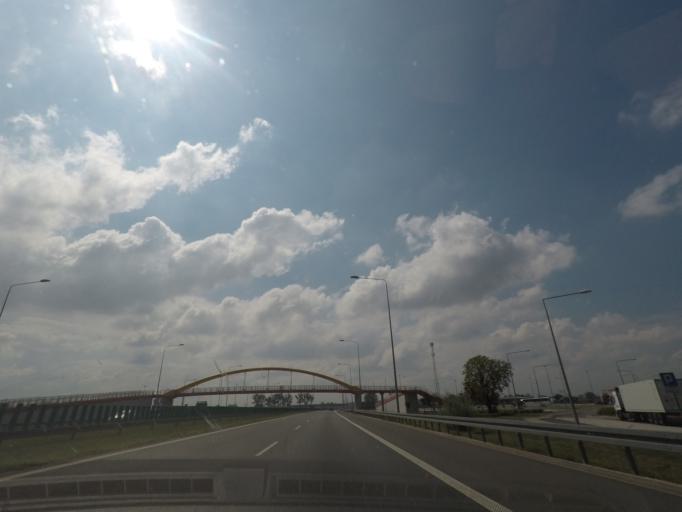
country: PL
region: Lodz Voivodeship
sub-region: Powiat kutnowski
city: Krzyzanow
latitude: 52.1873
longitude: 19.4873
